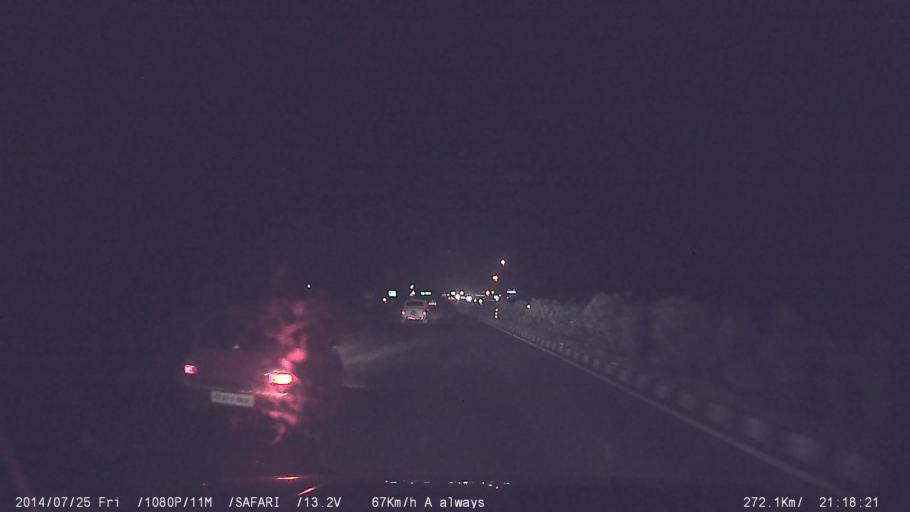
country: IN
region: Tamil Nadu
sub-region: Erode
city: Perundurai
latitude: 11.3060
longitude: 77.6033
